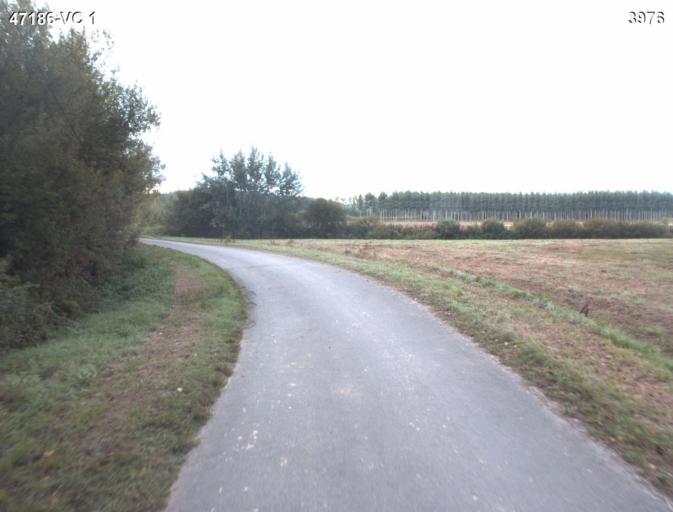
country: FR
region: Aquitaine
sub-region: Departement du Lot-et-Garonne
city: Port-Sainte-Marie
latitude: 44.2211
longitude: 0.4426
